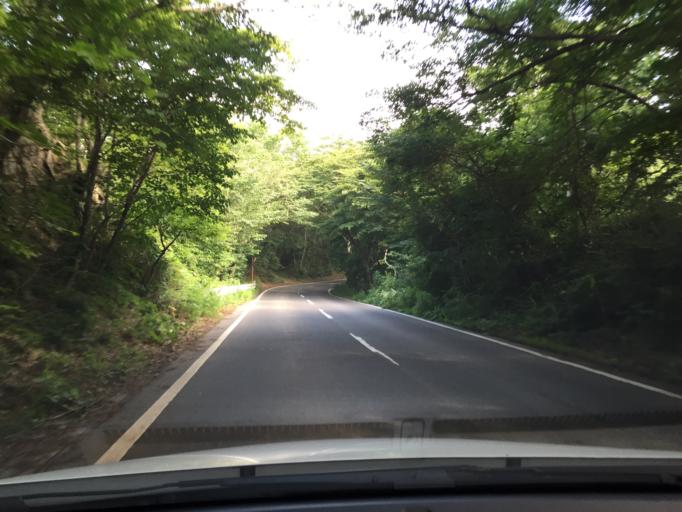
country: JP
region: Tochigi
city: Kuroiso
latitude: 37.2210
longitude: 140.0951
